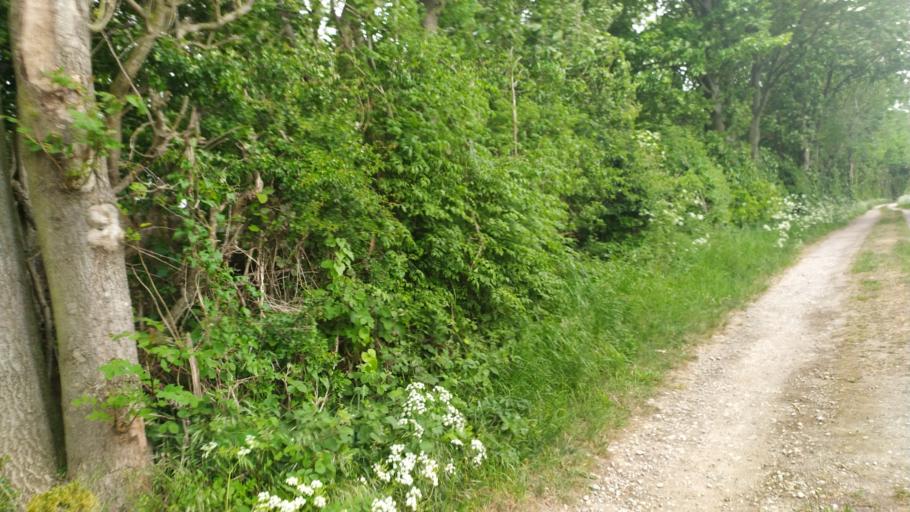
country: GB
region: England
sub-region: City and Borough of Leeds
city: Thorner
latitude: 53.8656
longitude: -1.3968
